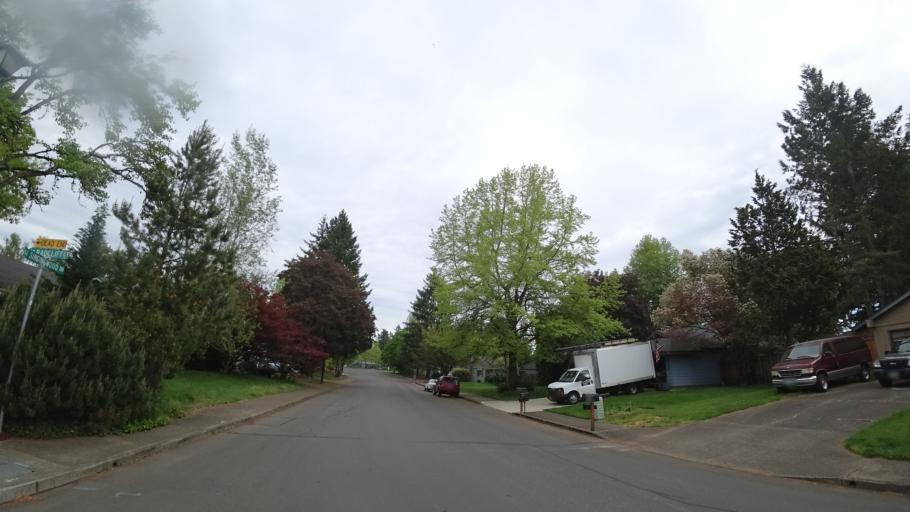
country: US
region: Oregon
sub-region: Washington County
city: Hillsboro
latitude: 45.4937
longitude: -122.9544
